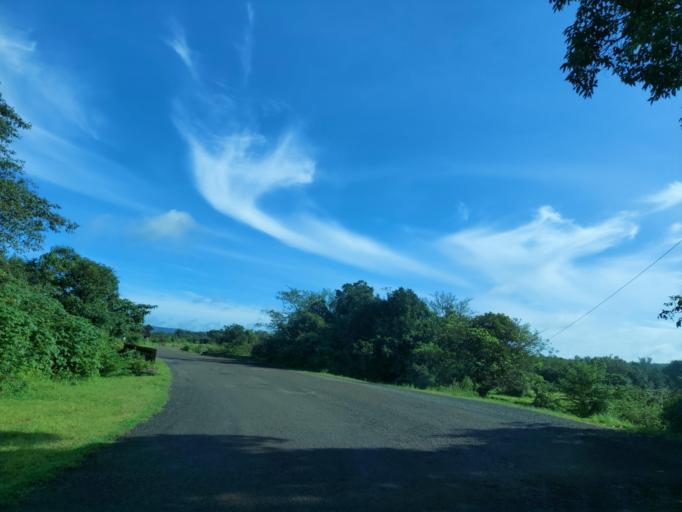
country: IN
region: Maharashtra
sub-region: Kolhapur
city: Ajra
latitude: 16.0195
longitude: 74.0533
